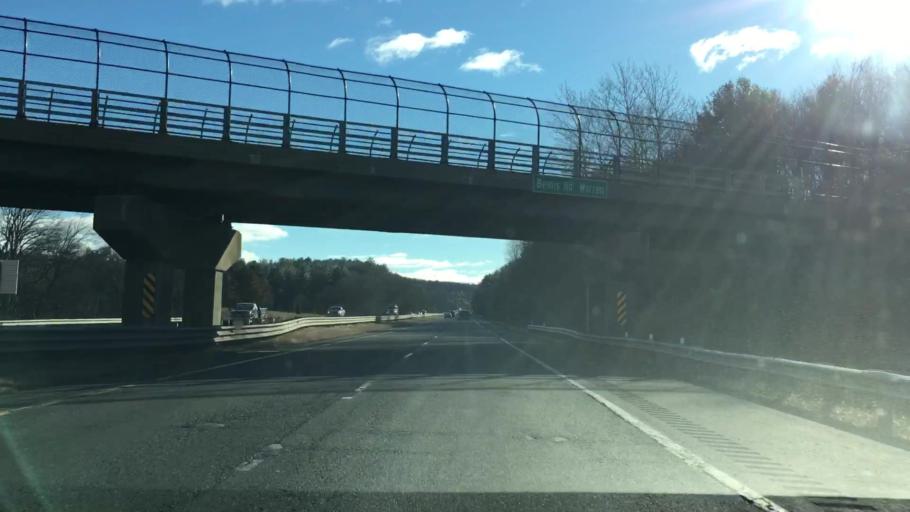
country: US
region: Massachusetts
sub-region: Worcester County
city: Warren
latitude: 42.1731
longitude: -72.1915
